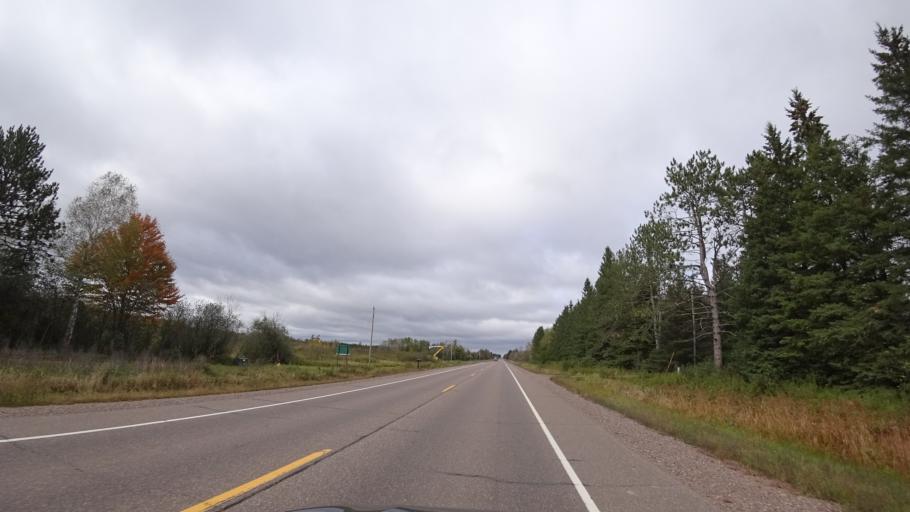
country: US
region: Wisconsin
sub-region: Rusk County
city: Ladysmith
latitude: 45.4926
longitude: -91.1115
